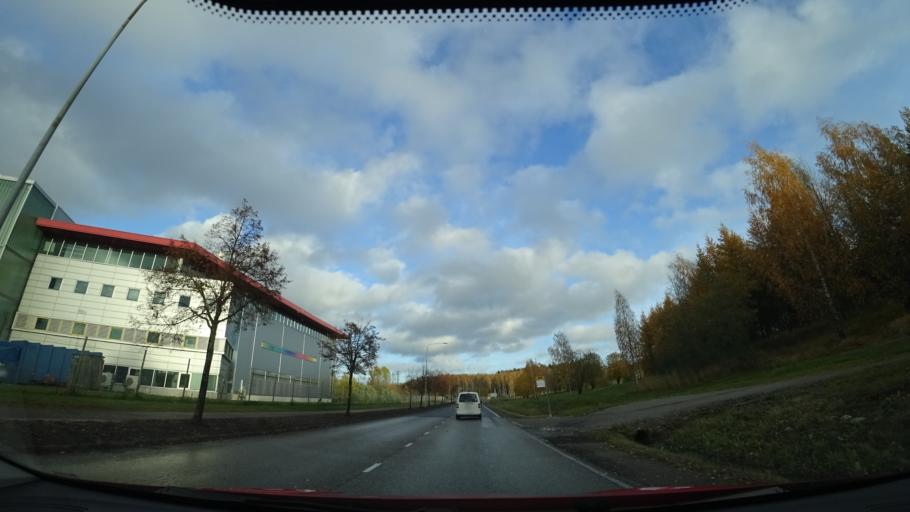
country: FI
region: Uusimaa
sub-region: Helsinki
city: Vantaa
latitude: 60.2858
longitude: 25.0535
